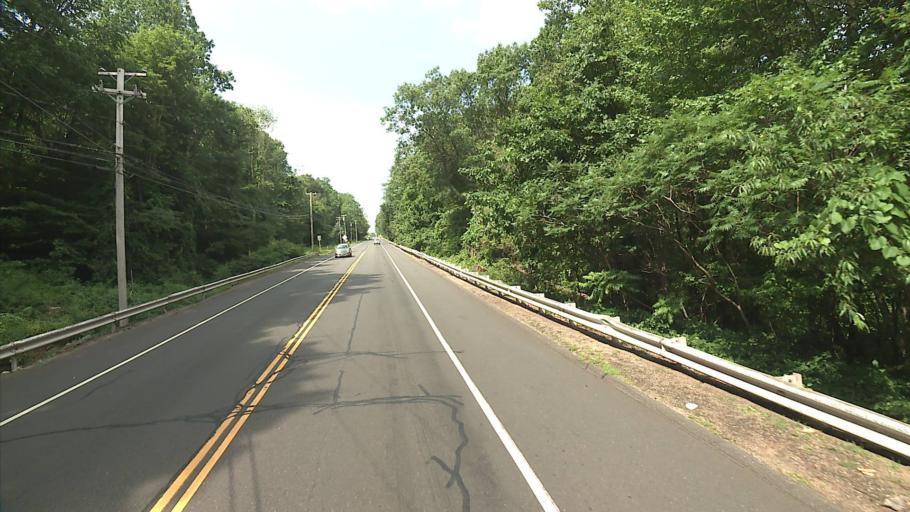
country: US
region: Connecticut
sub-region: New Haven County
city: Wolcott
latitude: 41.5616
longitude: -72.9388
